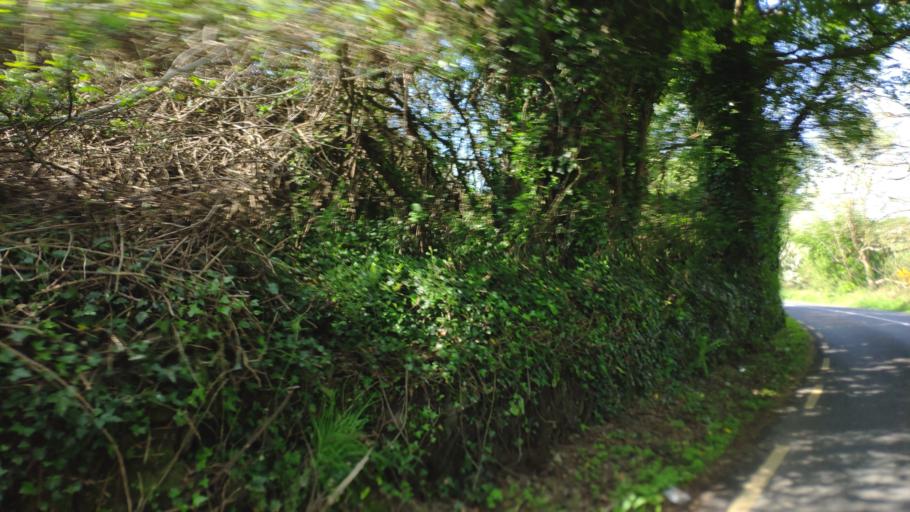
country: IE
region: Munster
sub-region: County Cork
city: Cork
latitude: 51.9234
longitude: -8.4949
